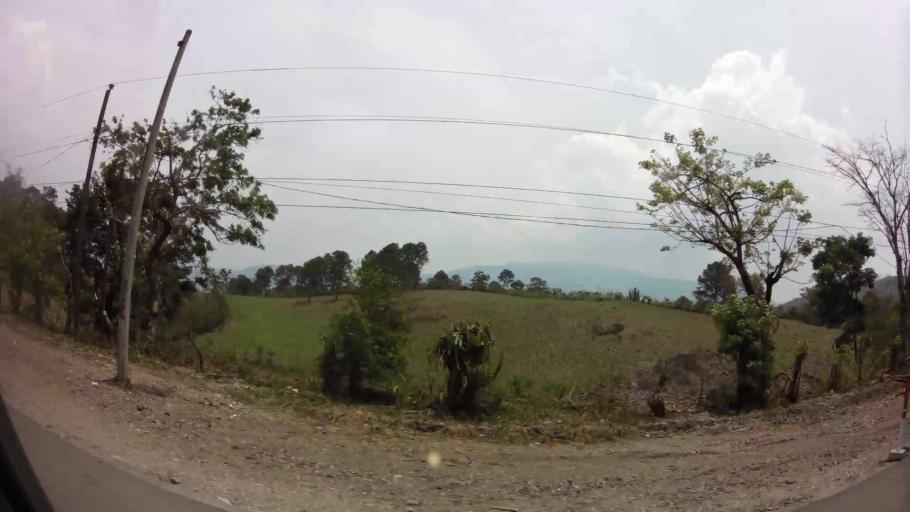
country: HN
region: Comayagua
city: Taulabe
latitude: 14.6759
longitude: -87.9534
